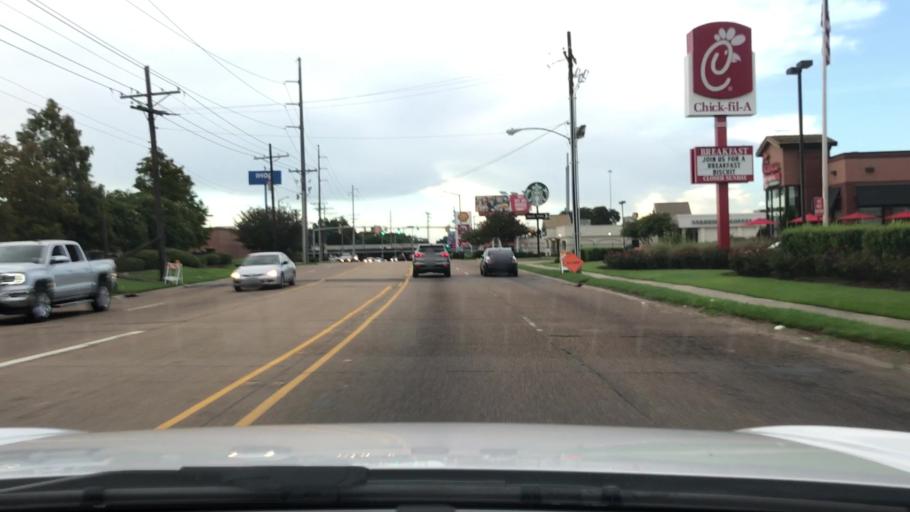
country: US
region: Louisiana
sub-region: East Baton Rouge Parish
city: Baton Rouge
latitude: 30.4196
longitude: -91.1411
